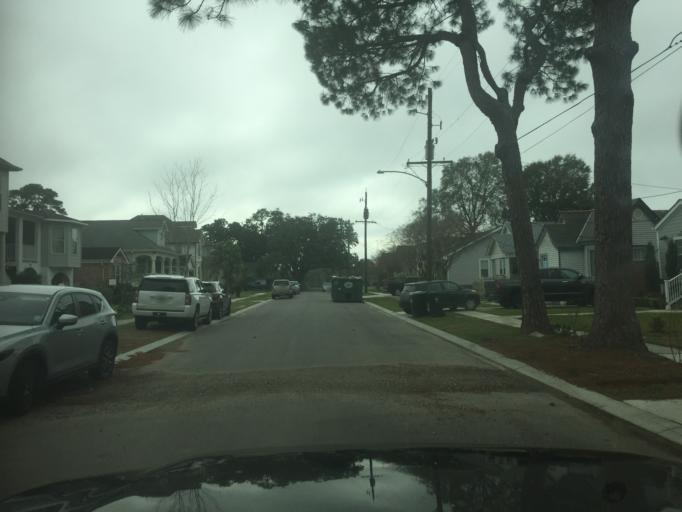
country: US
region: Louisiana
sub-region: Jefferson Parish
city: Metairie
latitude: 29.9975
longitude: -90.1112
